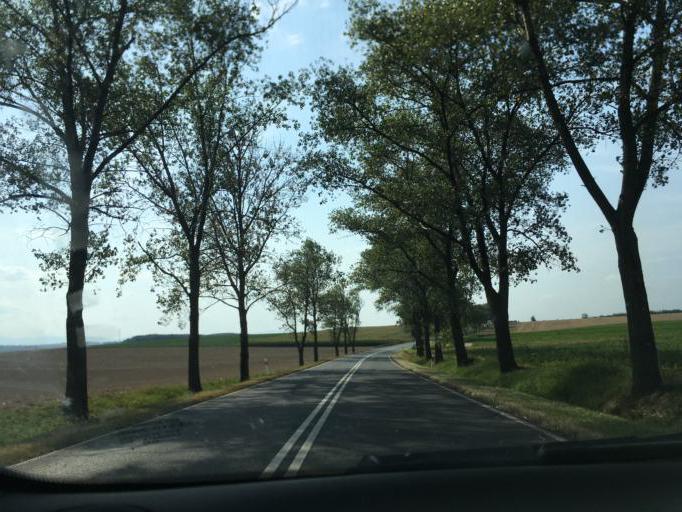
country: PL
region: Opole Voivodeship
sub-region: Powiat prudnicki
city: Moszczanka
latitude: 50.4196
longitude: 17.4726
